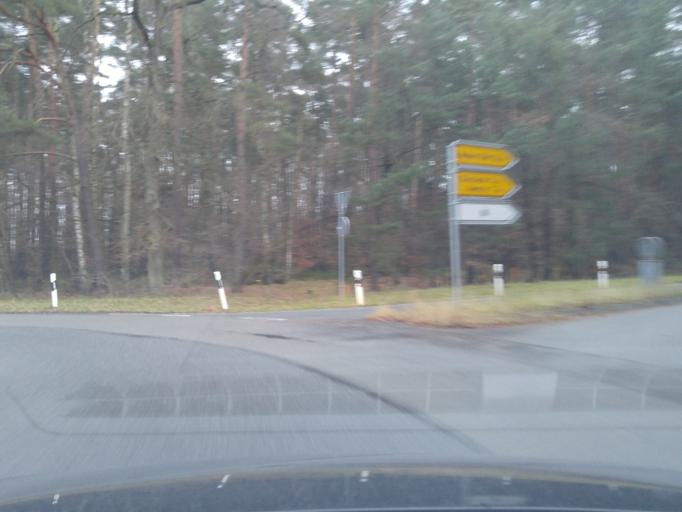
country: DE
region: Lower Saxony
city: Barendorf
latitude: 53.2544
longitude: 10.5272
